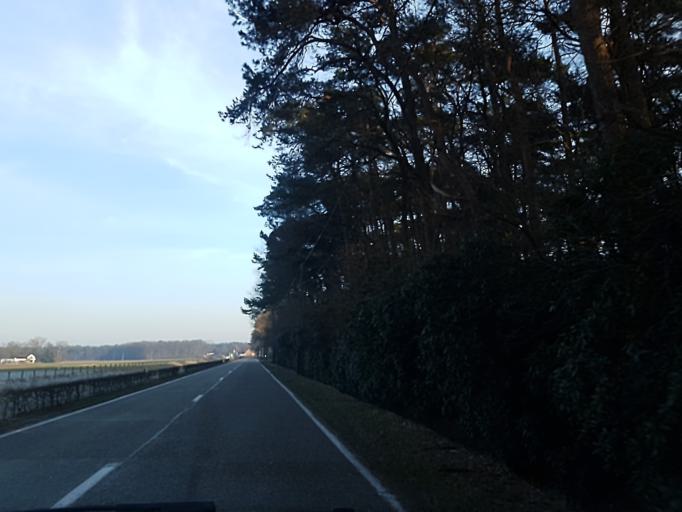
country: BE
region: Flanders
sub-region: Provincie Antwerpen
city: Zoersel
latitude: 51.2689
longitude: 4.6738
